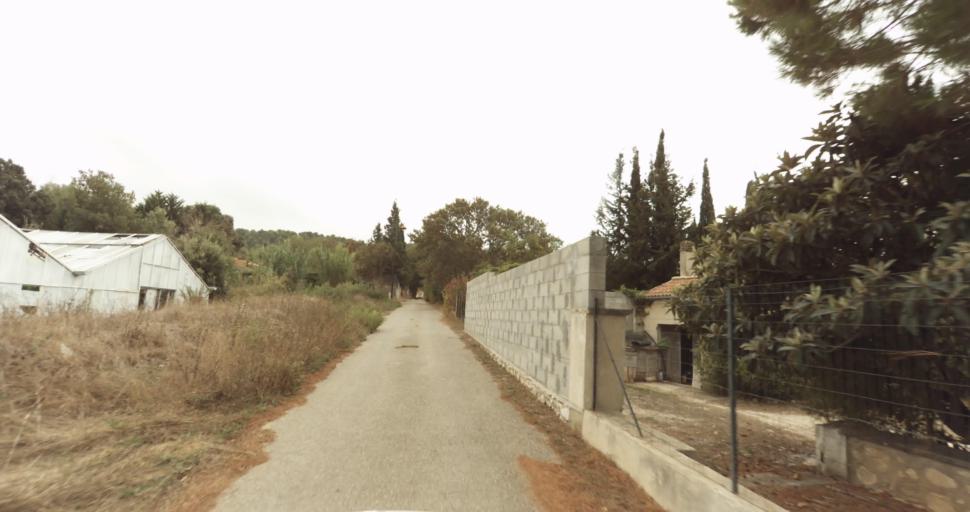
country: FR
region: Provence-Alpes-Cote d'Azur
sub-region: Departement des Bouches-du-Rhone
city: Saint-Victoret
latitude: 43.4132
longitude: 5.2704
